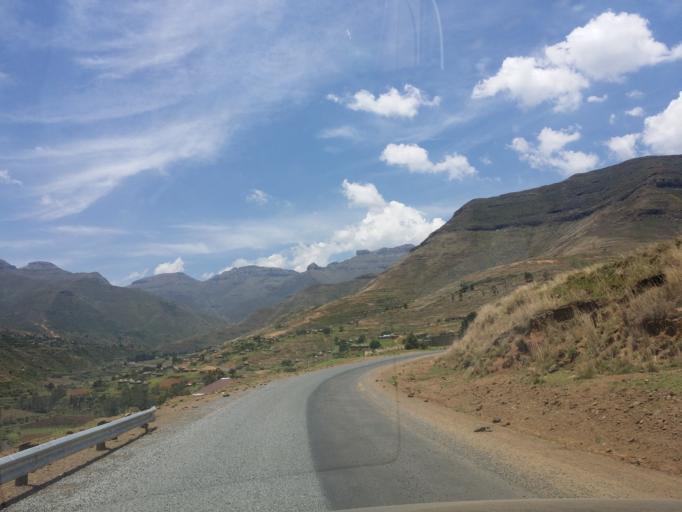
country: LS
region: Butha-Buthe
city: Butha-Buthe
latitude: -28.7577
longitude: 28.5269
